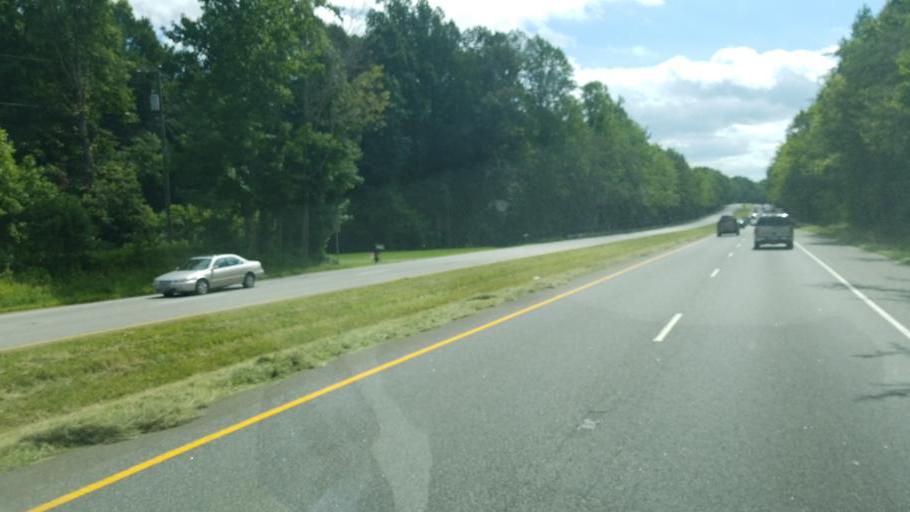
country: US
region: Virginia
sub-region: Stafford County
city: Falmouth
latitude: 38.4068
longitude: -77.5883
